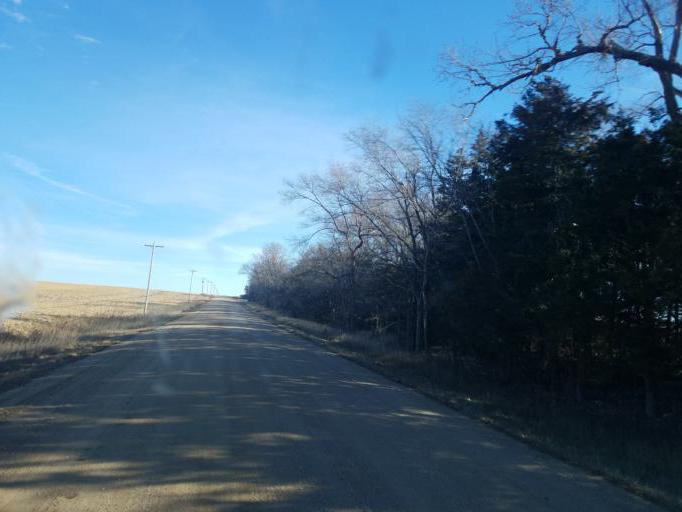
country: US
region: Nebraska
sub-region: Knox County
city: Center
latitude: 42.6263
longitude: -97.7990
